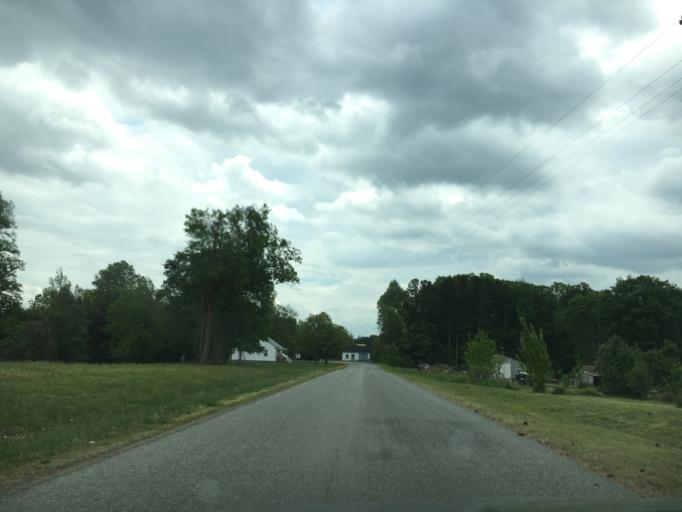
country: US
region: Virginia
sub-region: Halifax County
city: Halifax
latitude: 36.7988
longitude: -78.9416
